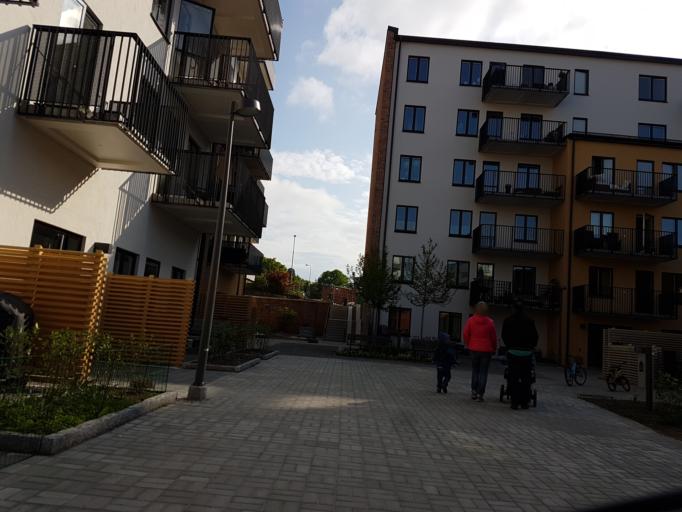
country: SE
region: Stockholm
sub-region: Sundbybergs Kommun
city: Sundbyberg
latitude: 59.3635
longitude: 17.9527
